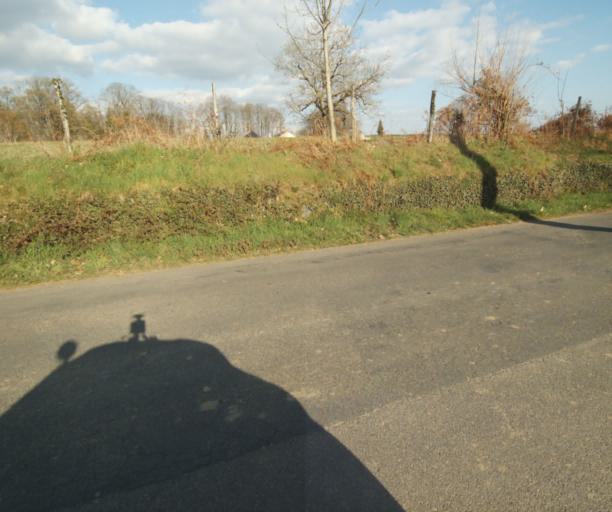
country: FR
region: Limousin
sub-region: Departement de la Correze
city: Saint-Clement
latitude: 45.3474
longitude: 1.6383
